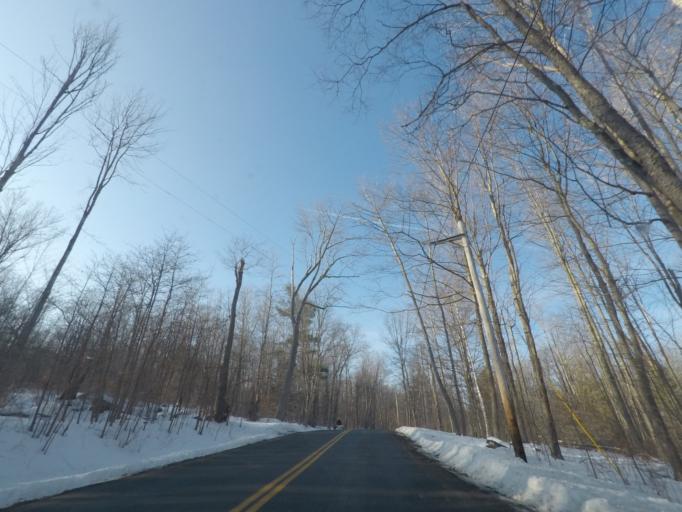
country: US
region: Massachusetts
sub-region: Berkshire County
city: Richmond
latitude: 42.5212
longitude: -73.3782
